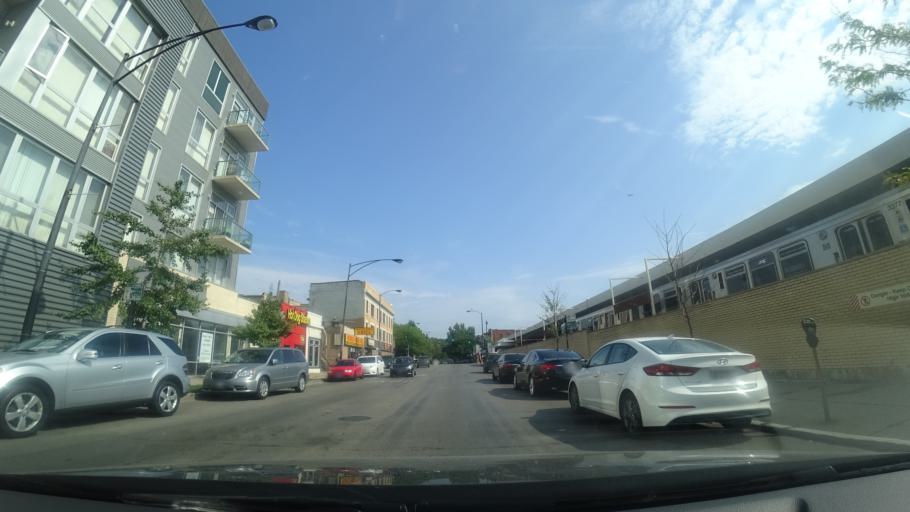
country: US
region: Illinois
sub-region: Cook County
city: Lincolnwood
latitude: 41.9676
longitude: -87.7133
